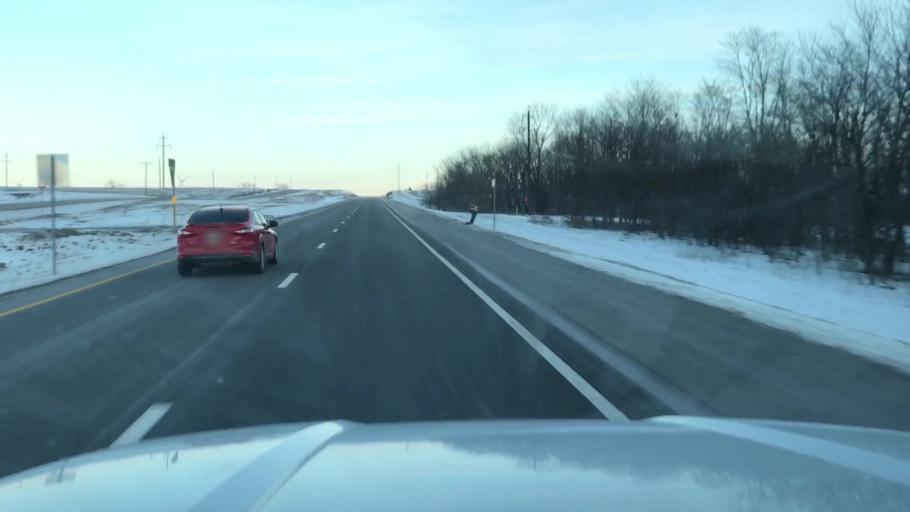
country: US
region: Missouri
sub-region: DeKalb County
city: Maysville
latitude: 39.7619
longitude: -94.4554
